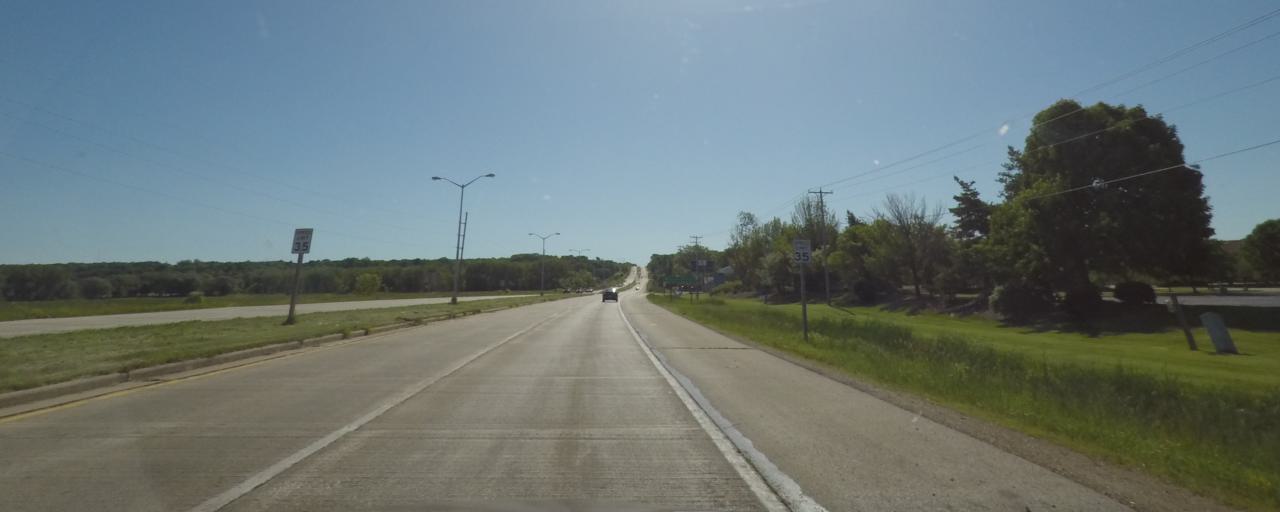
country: US
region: Wisconsin
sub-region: Fond du Lac County
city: Fond du Lac
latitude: 43.7837
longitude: -88.3988
